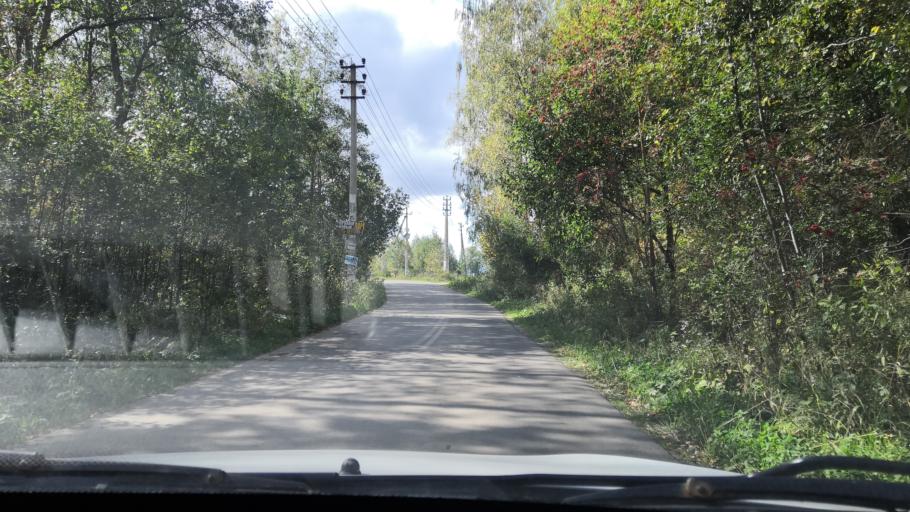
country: RU
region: Moskovskaya
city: Povarovo
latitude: 56.0644
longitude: 37.0340
